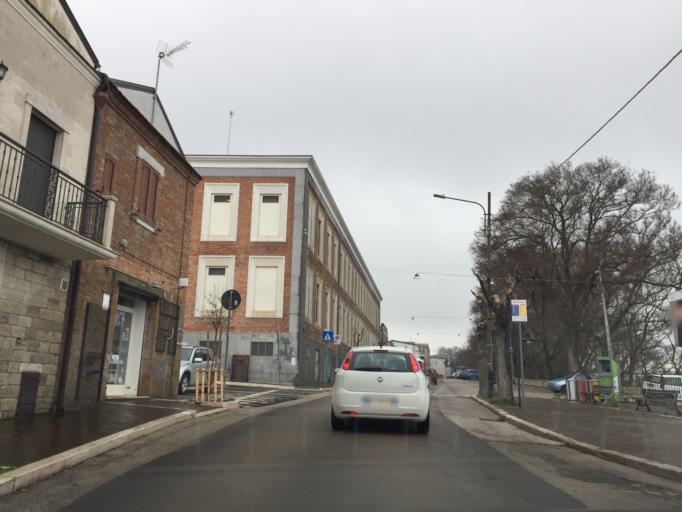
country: IT
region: Apulia
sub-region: Provincia di Foggia
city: Troia
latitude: 41.3629
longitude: 15.3106
